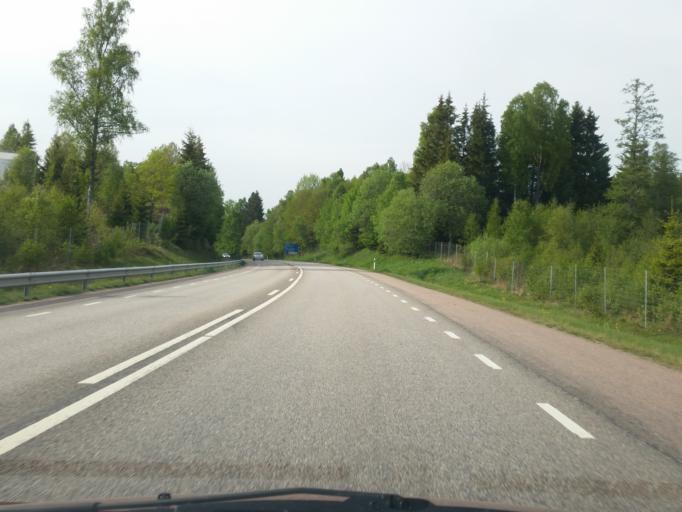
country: SE
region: Vaestra Goetaland
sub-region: Ulricehamns Kommun
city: Ulricehamn
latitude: 57.8094
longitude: 13.2971
